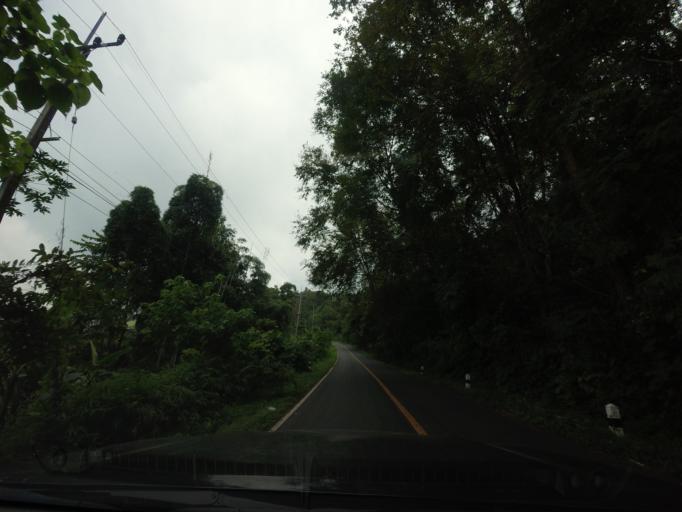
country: TH
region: Nan
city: Pua
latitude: 19.1884
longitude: 101.0203
